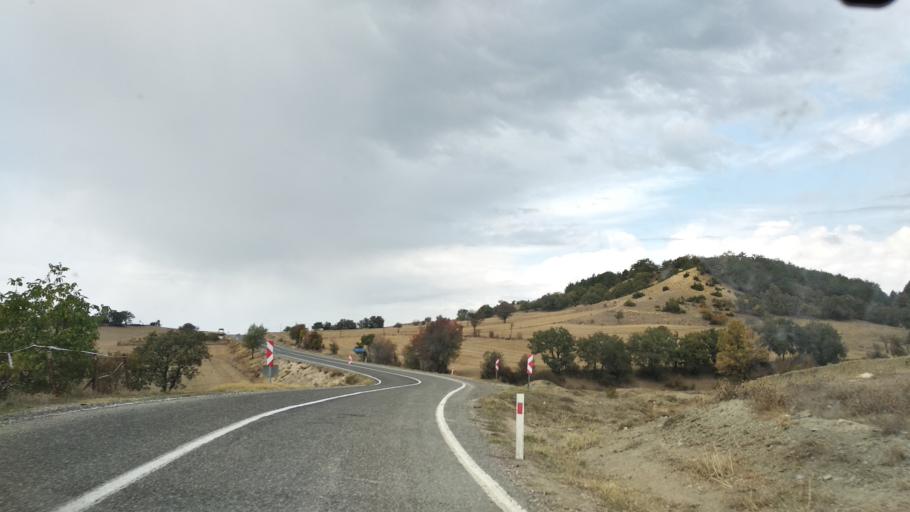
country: TR
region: Bolu
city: Seben
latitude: 40.3329
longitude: 31.4649
